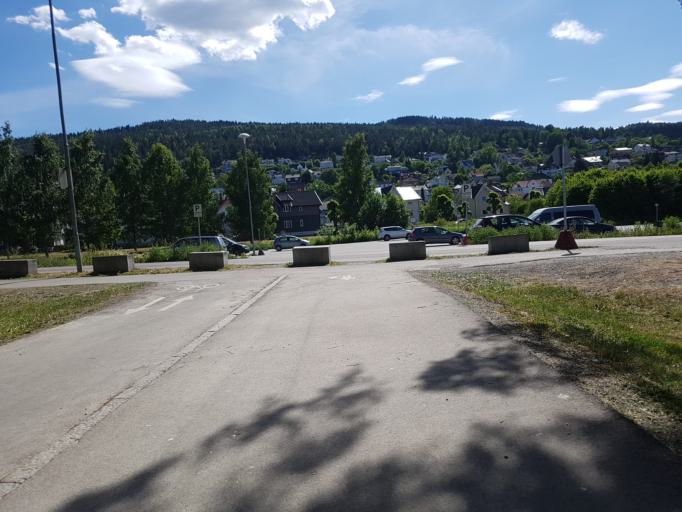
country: NO
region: Buskerud
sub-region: Drammen
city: Drammen
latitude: 59.7394
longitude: 10.1822
